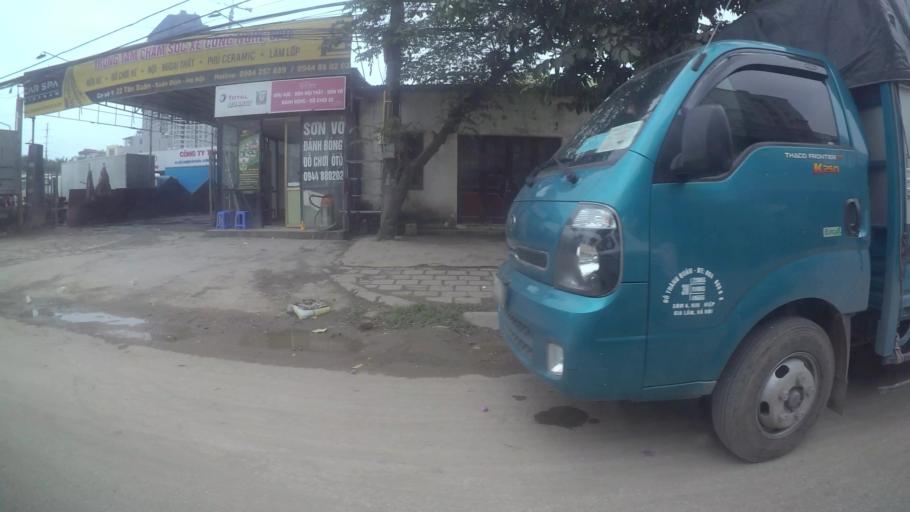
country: VN
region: Ha Noi
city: Tay Ho
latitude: 21.0839
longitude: 105.7856
